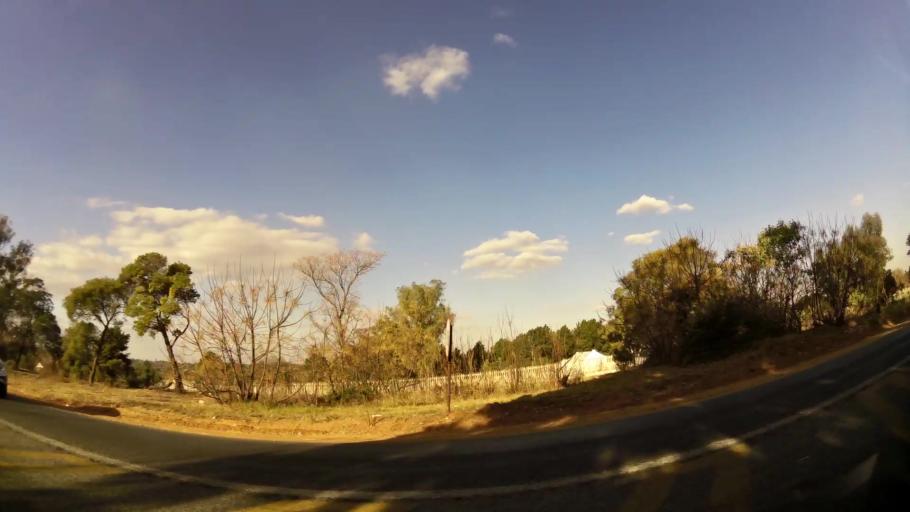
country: ZA
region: Gauteng
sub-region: City of Johannesburg Metropolitan Municipality
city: Midrand
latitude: -25.9730
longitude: 28.1357
